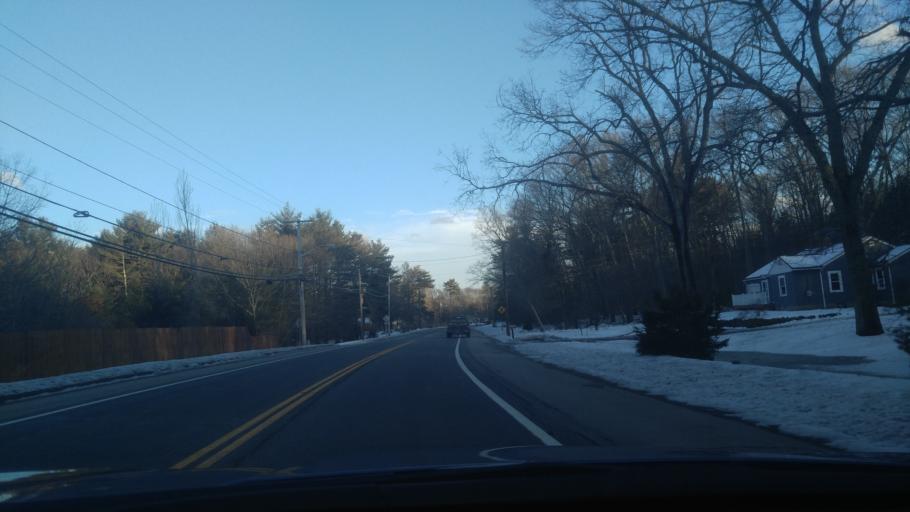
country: US
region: Rhode Island
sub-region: Kent County
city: Coventry
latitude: 41.7105
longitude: -71.6491
